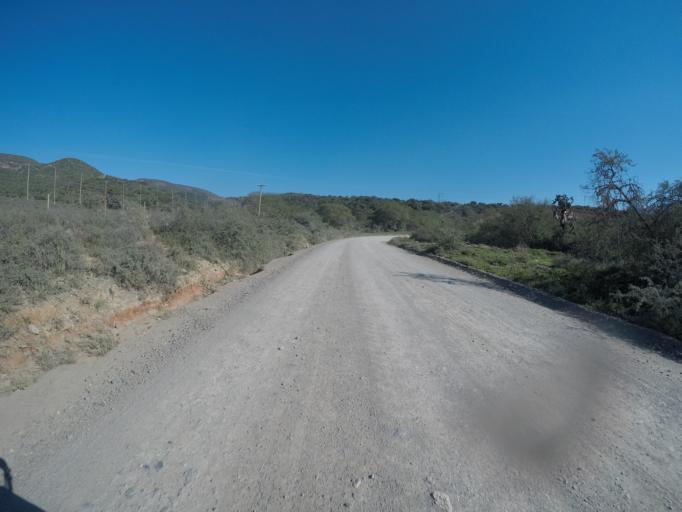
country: ZA
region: Eastern Cape
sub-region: Cacadu District Municipality
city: Kruisfontein
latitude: -33.6742
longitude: 24.5767
